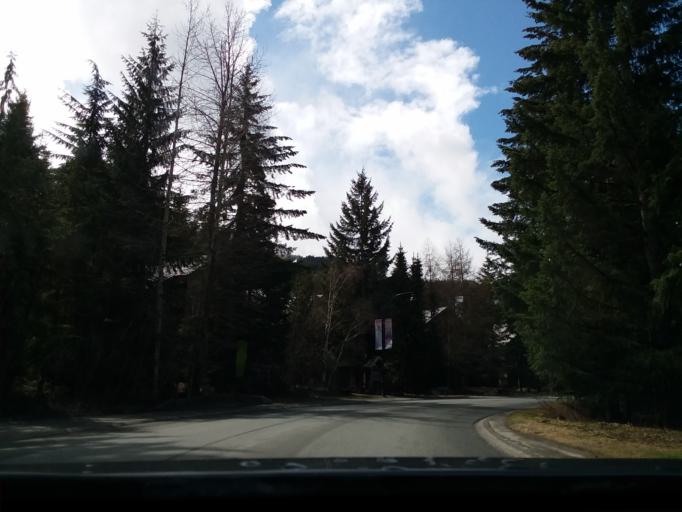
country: CA
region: British Columbia
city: Whistler
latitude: 50.1137
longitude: -122.9495
